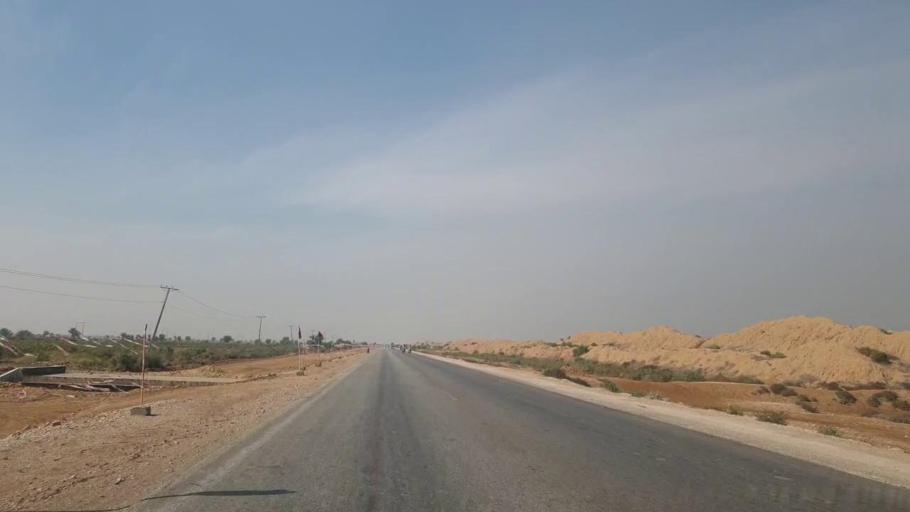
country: PK
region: Sindh
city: Sann
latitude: 26.0086
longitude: 68.1516
